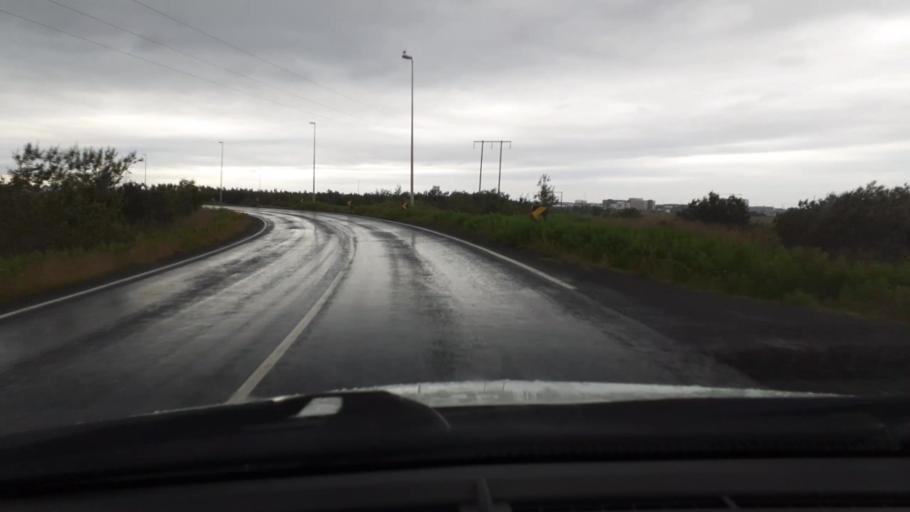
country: IS
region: West
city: Akranes
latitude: 64.3311
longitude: -22.0372
